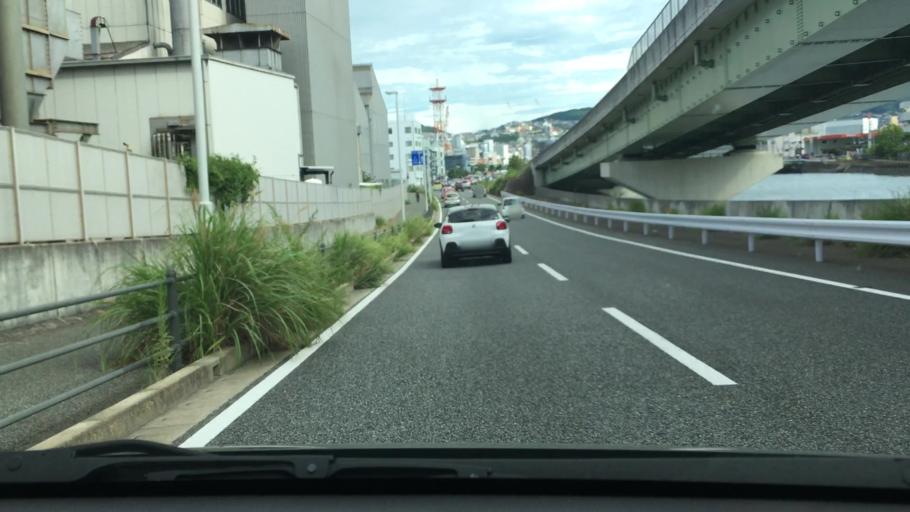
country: JP
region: Nagasaki
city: Nagasaki-shi
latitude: 32.7591
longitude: 129.8634
